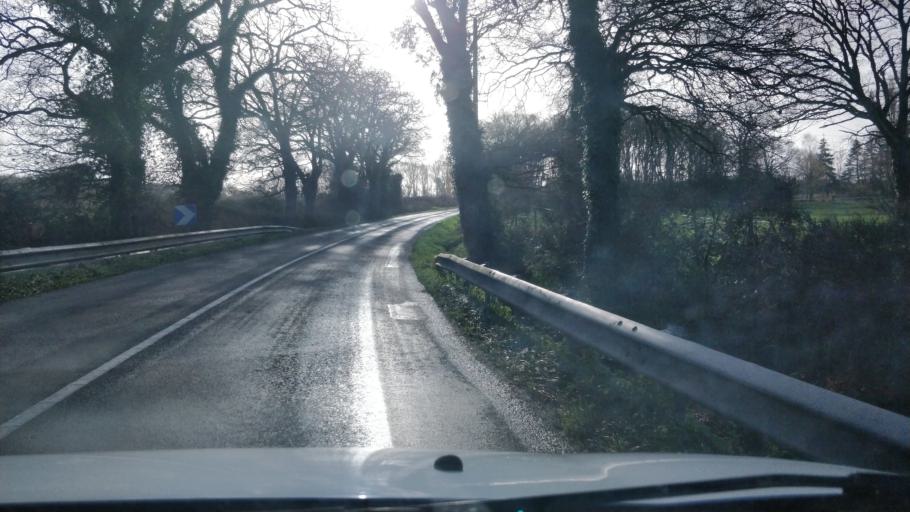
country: FR
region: Pays de la Loire
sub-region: Departement de la Loire-Atlantique
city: Saint-Molf
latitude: 47.3684
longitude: -2.4318
